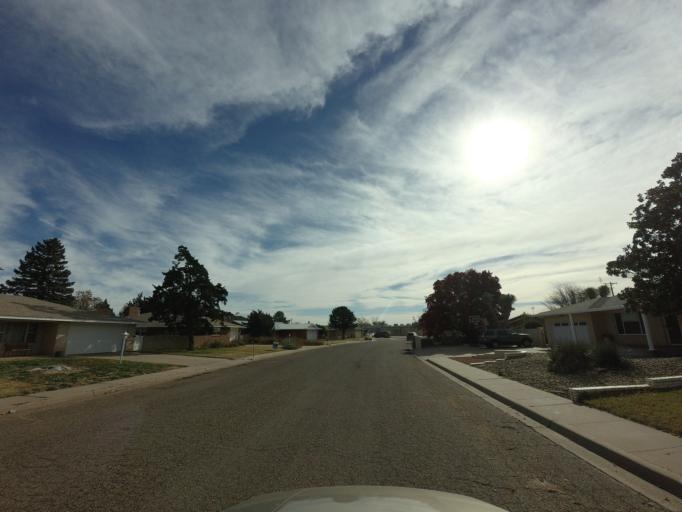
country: US
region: New Mexico
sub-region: Curry County
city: Clovis
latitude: 34.4156
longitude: -103.1906
